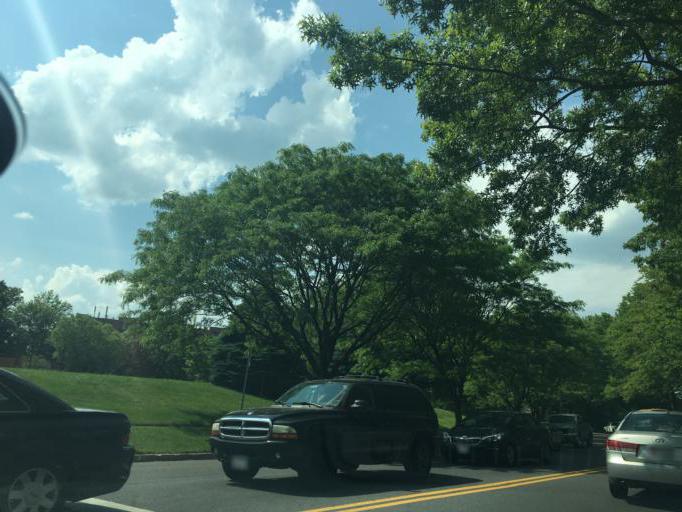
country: US
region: Maryland
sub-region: Montgomery County
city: Montgomery Village
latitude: 39.1727
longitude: -77.2015
